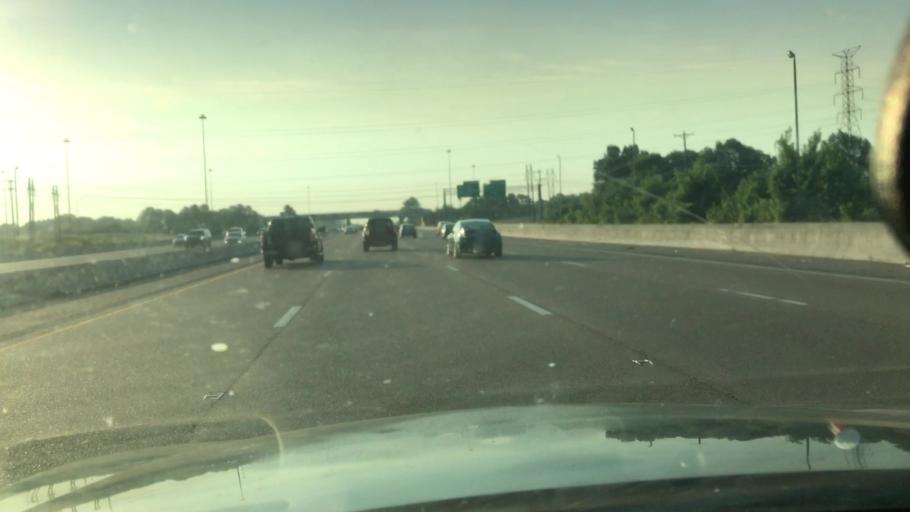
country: US
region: Mississippi
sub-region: De Soto County
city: Southaven
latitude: 35.0803
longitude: -89.9348
